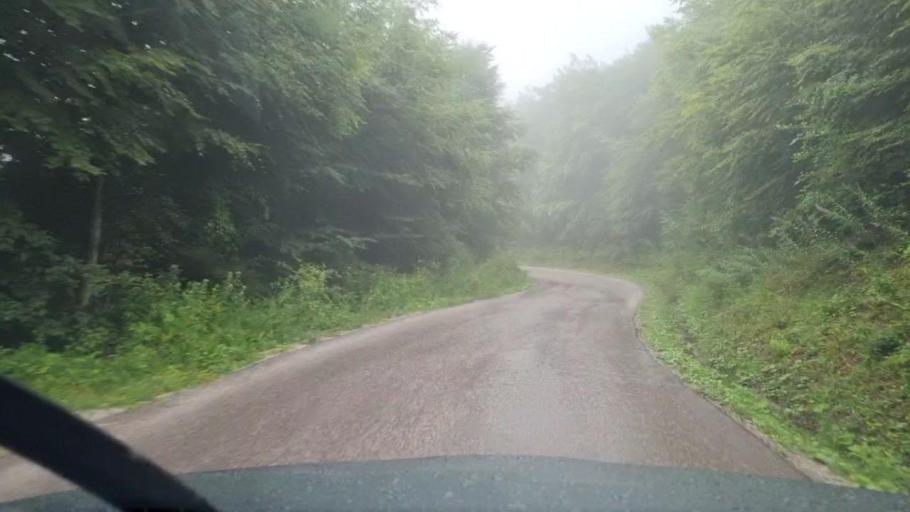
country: BA
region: Republika Srpska
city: Koran
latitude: 43.6423
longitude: 18.6150
